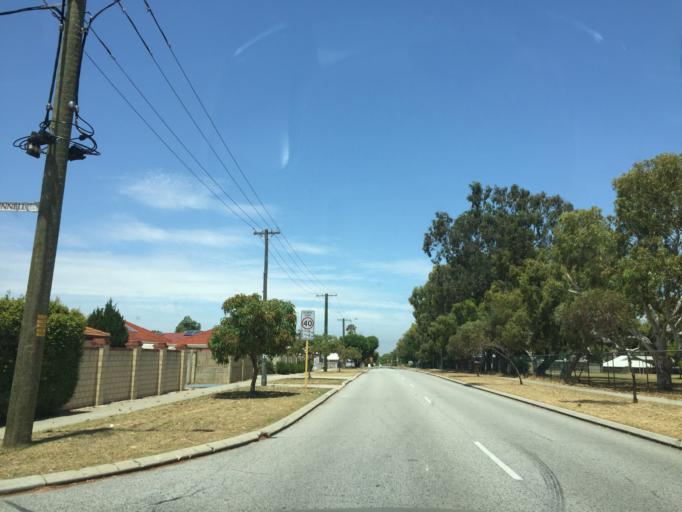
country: AU
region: Western Australia
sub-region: Canning
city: Queens Park
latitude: -31.9981
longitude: 115.9460
